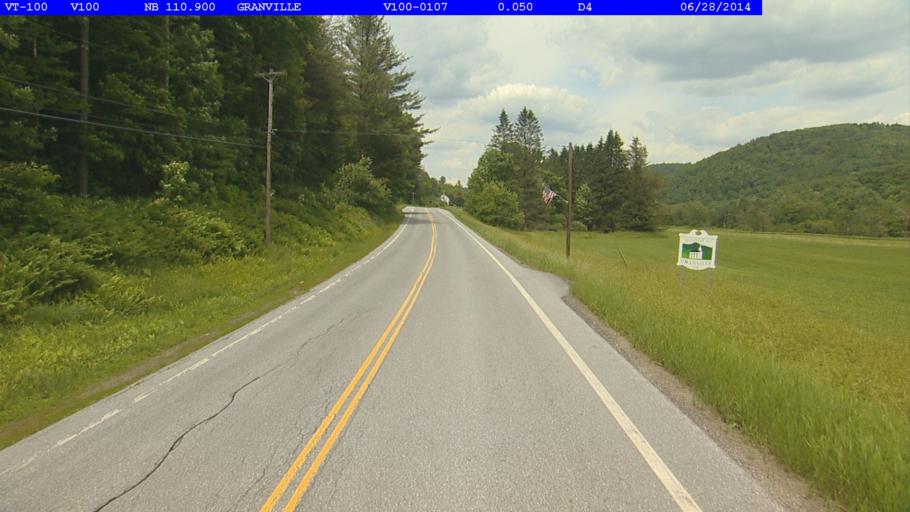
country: US
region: Vermont
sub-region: Orange County
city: Randolph
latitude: 43.9455
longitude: -72.8405
